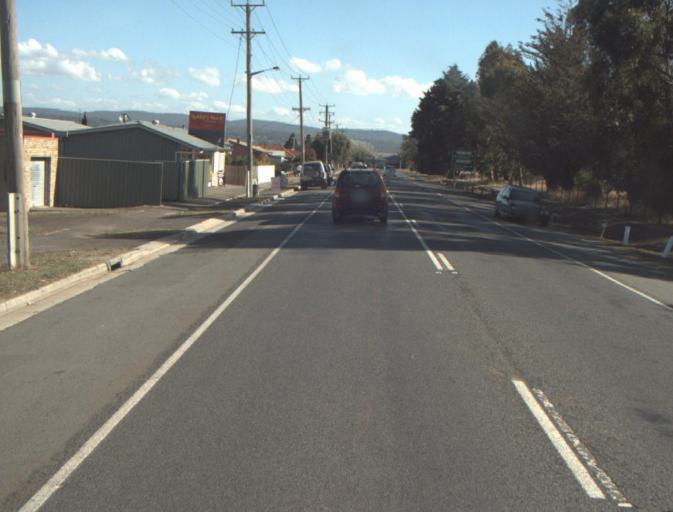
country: AU
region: Tasmania
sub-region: Launceston
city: Mayfield
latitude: -41.3769
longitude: 147.1297
